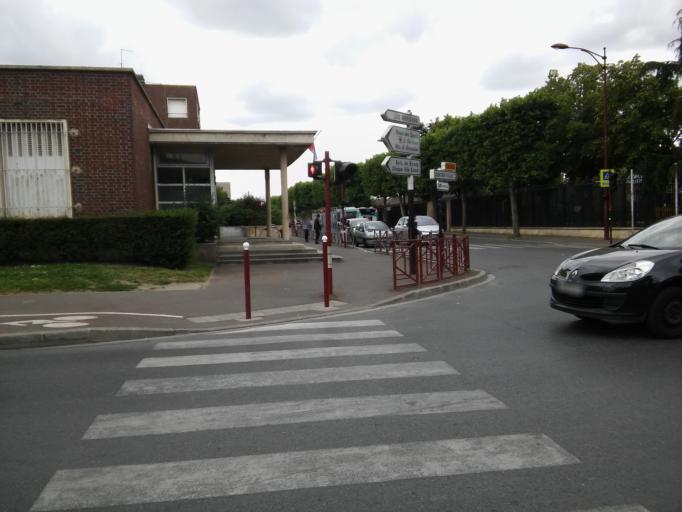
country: FR
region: Ile-de-France
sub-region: Departement de Seine-Saint-Denis
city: Bondy
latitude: 48.9122
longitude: 2.4817
